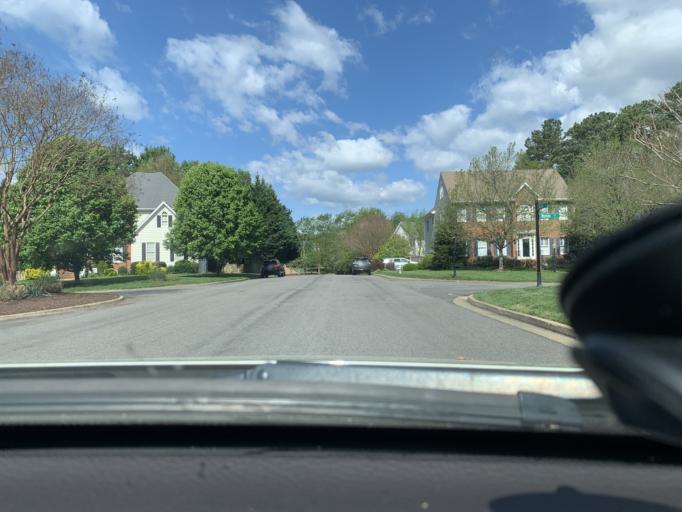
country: US
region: Virginia
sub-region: Henrico County
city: Tuckahoe
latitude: 37.5921
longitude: -77.6014
